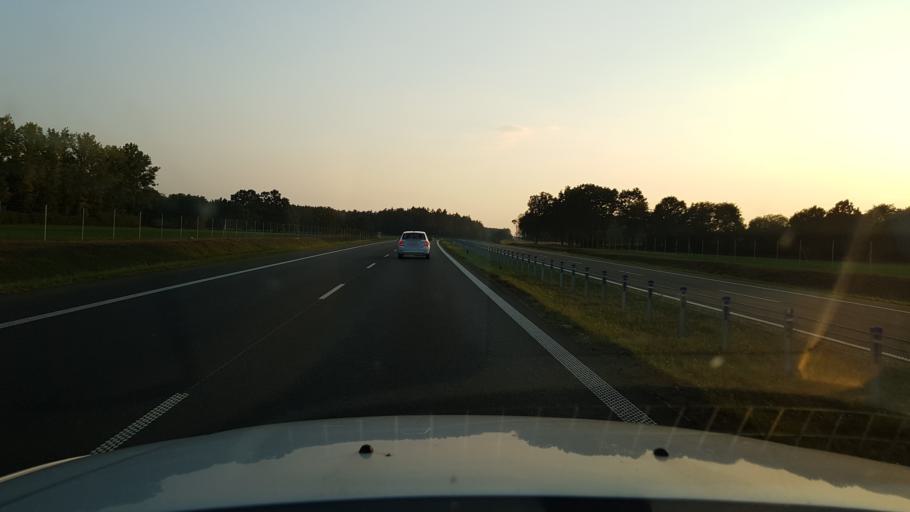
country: PL
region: West Pomeranian Voivodeship
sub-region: Powiat gryficki
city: Ploty
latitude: 53.8325
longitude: 15.2938
